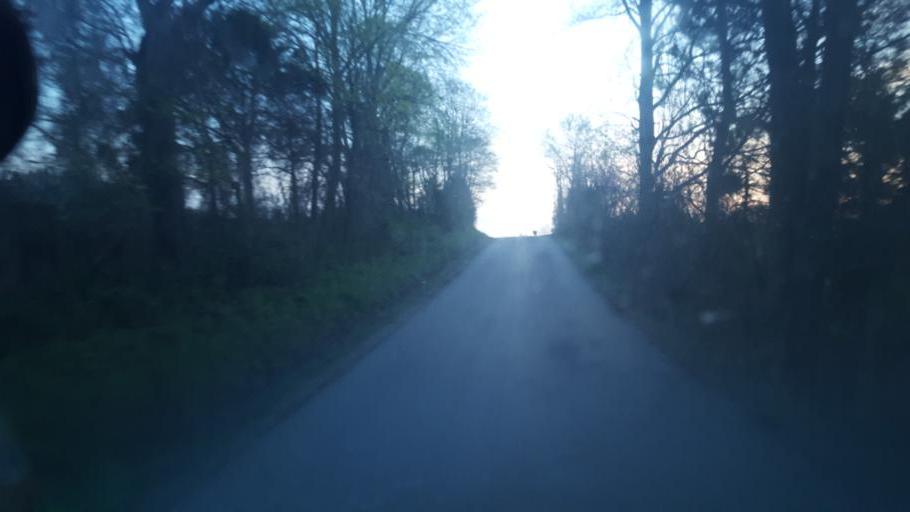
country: US
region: Kentucky
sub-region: Hart County
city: Munfordville
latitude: 37.2579
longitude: -85.9716
